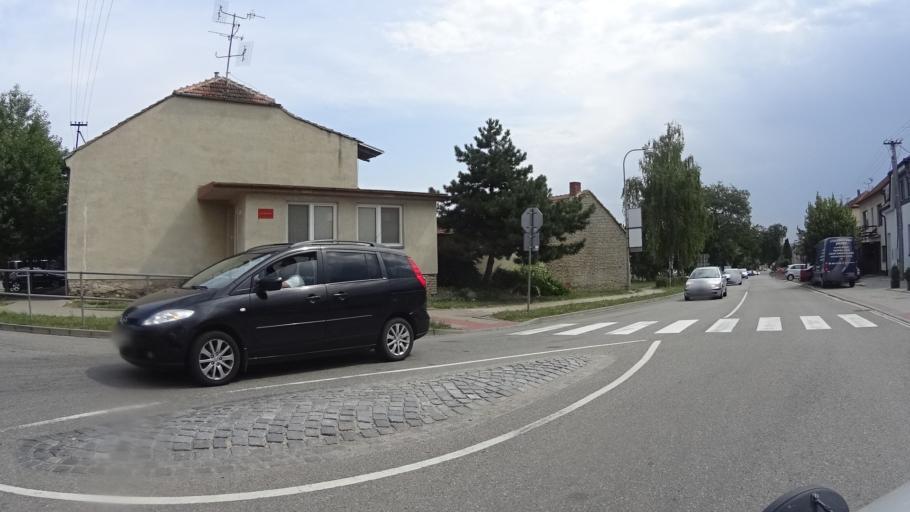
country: CZ
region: South Moravian
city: Podivin
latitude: 48.8291
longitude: 16.8476
